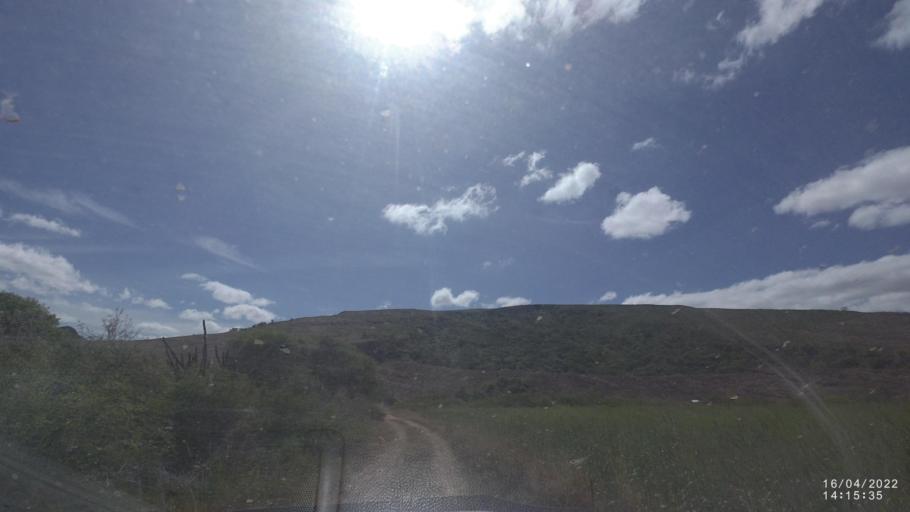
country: BO
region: Cochabamba
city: Mizque
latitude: -18.0569
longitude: -65.5102
